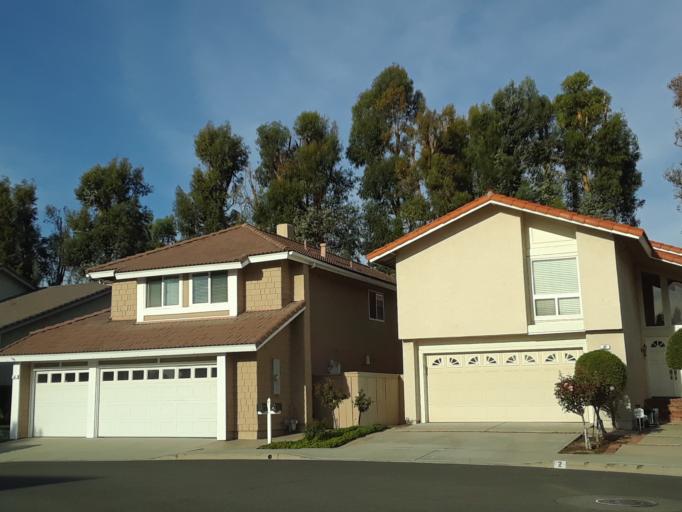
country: US
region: California
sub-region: Orange County
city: North Tustin
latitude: 33.7218
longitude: -117.7658
